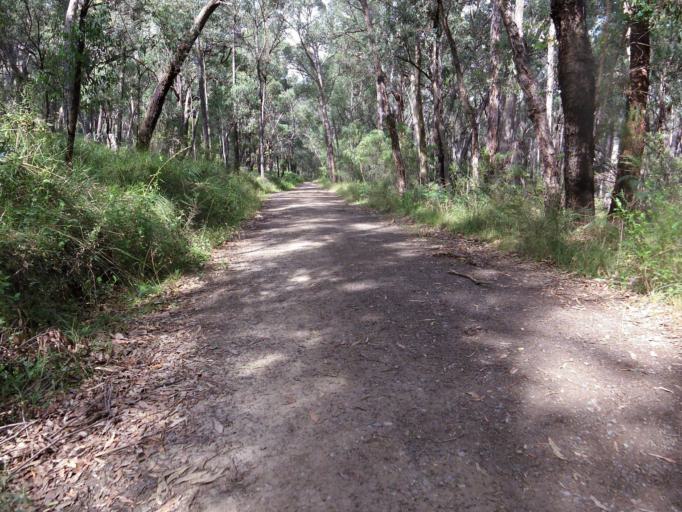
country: AU
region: Victoria
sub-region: Knox
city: The Basin
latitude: -37.8399
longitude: 145.3341
